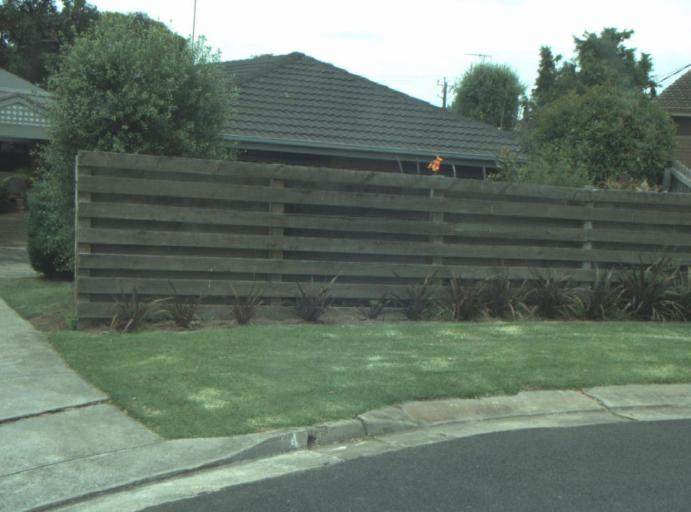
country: AU
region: Victoria
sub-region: Greater Geelong
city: Wandana Heights
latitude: -38.1872
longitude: 144.3316
